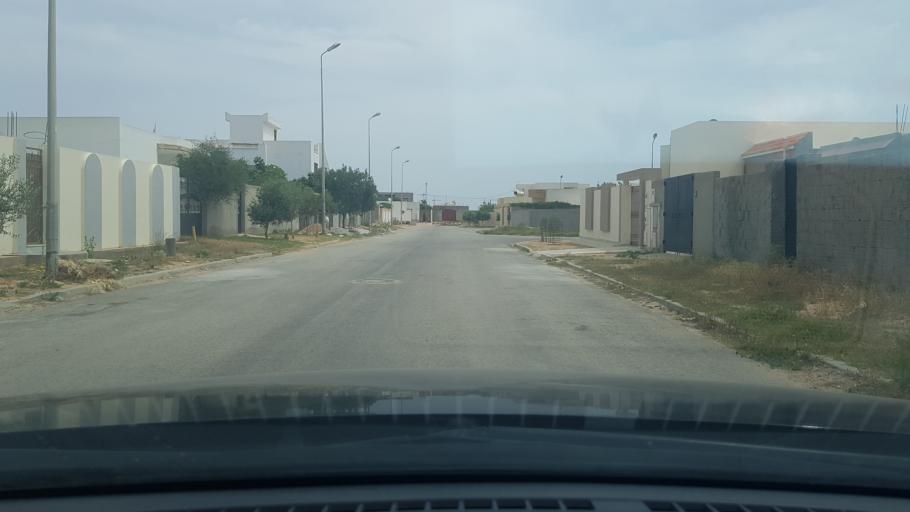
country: TN
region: Safaqis
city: Al Qarmadah
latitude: 34.8274
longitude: 10.7488
